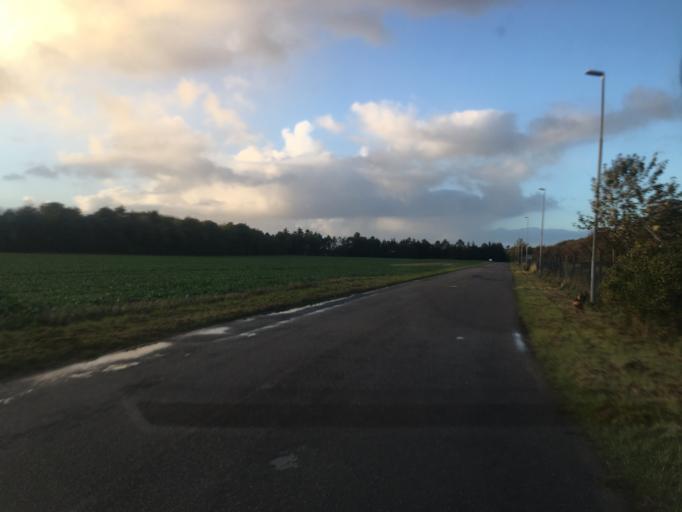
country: DK
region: South Denmark
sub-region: Tonder Kommune
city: Tonder
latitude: 54.9233
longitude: 8.8512
